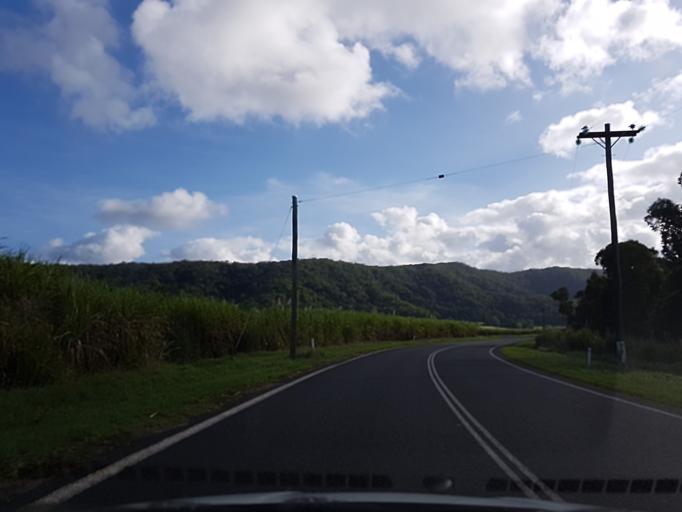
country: AU
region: Queensland
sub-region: Cairns
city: Port Douglas
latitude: -16.2791
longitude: 145.3821
